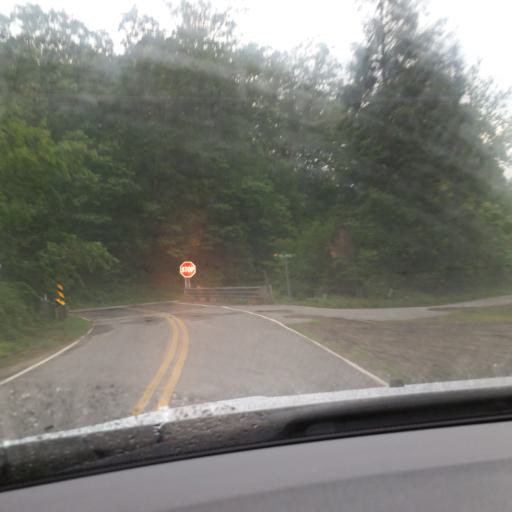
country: US
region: North Carolina
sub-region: Yancey County
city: Burnsville
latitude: 35.8315
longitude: -82.1963
